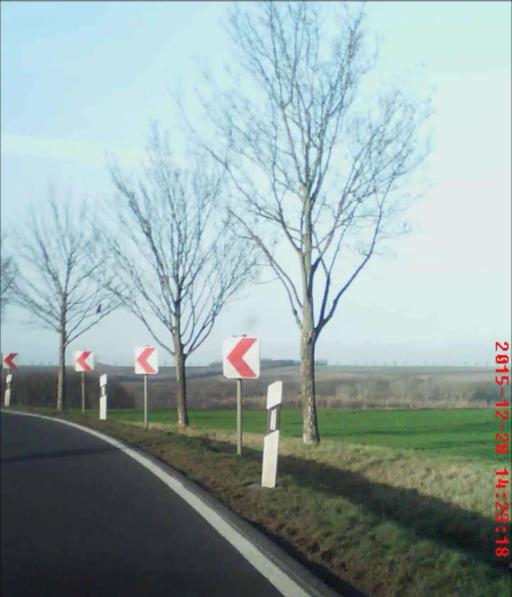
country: DE
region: Thuringia
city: Niederrossla
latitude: 51.0531
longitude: 11.4620
